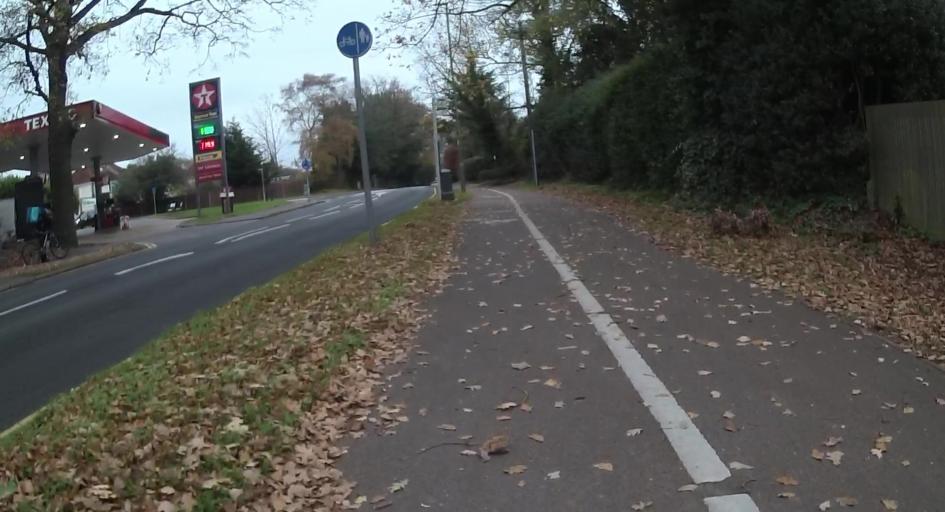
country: GB
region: England
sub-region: Surrey
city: Frimley
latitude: 51.3198
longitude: -0.7337
